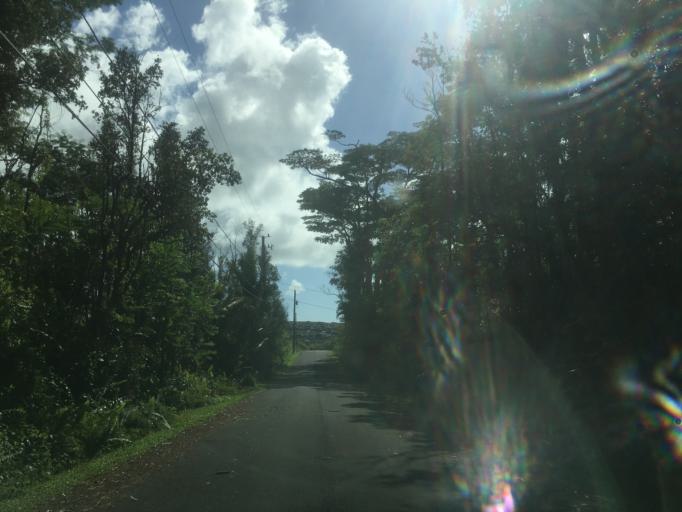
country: US
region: Hawaii
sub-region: Hawaii County
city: Leilani Estates
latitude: 19.4767
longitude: -154.9078
